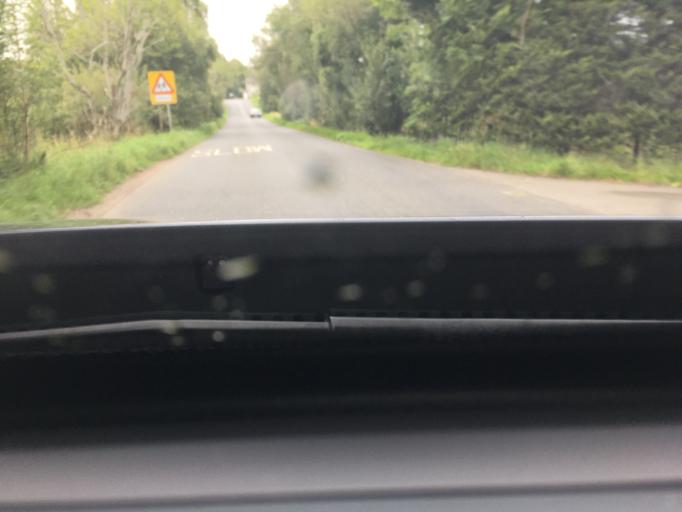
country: GB
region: Northern Ireland
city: Moy
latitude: 54.5153
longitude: -6.6317
